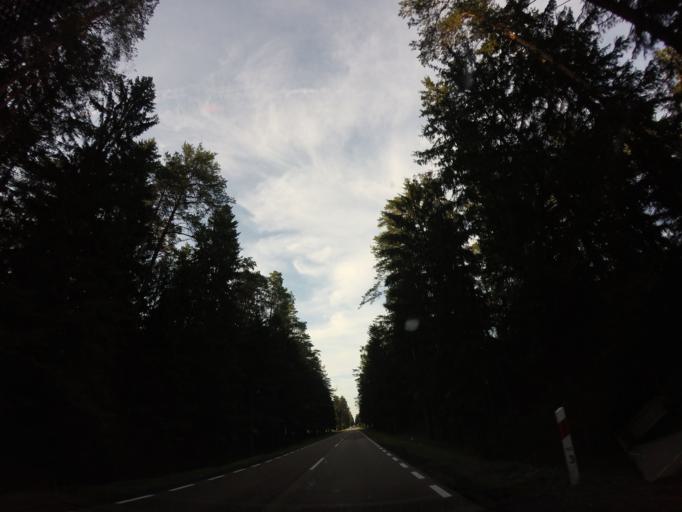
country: PL
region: Podlasie
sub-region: Powiat augustowski
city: Augustow
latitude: 53.9180
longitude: 23.1487
